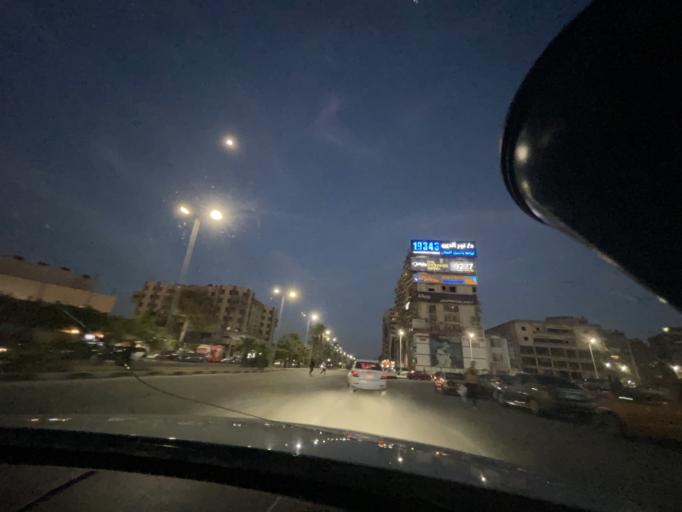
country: EG
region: Muhafazat al Qahirah
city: Cairo
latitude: 30.0705
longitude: 31.3550
